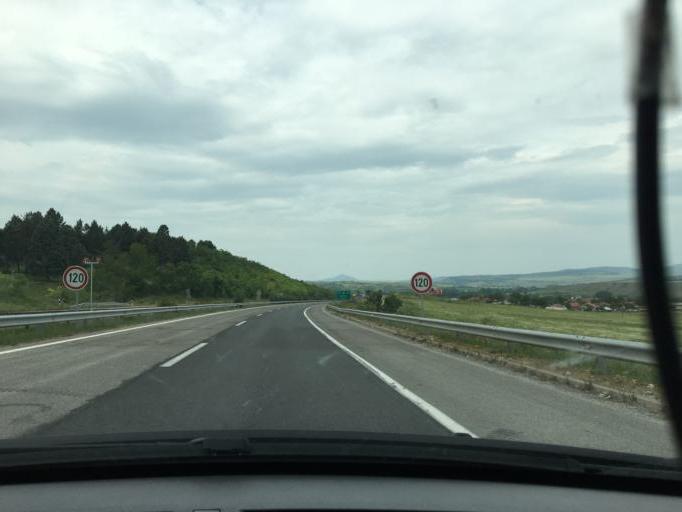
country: MK
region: Gradsko
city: Gradsko
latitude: 41.5756
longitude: 21.9325
